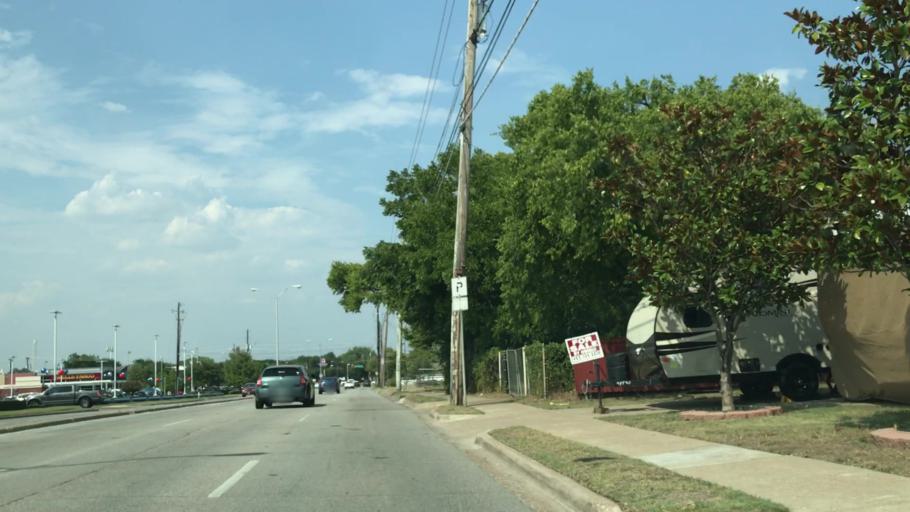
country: US
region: Texas
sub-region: Dallas County
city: University Park
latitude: 32.8280
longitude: -96.8284
